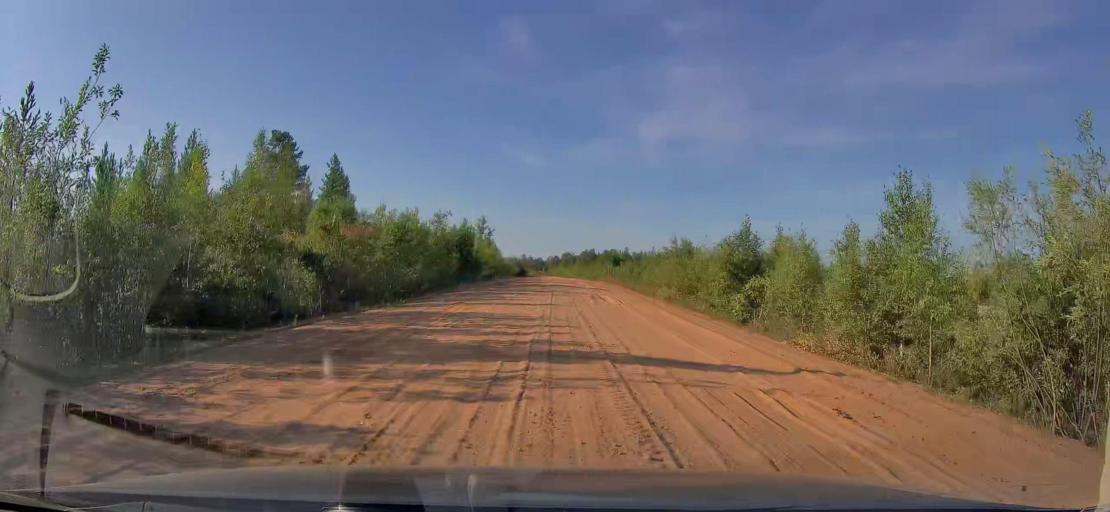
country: RU
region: Arkhangelskaya
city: Leshukonskoye
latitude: 65.2720
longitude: 45.2499
